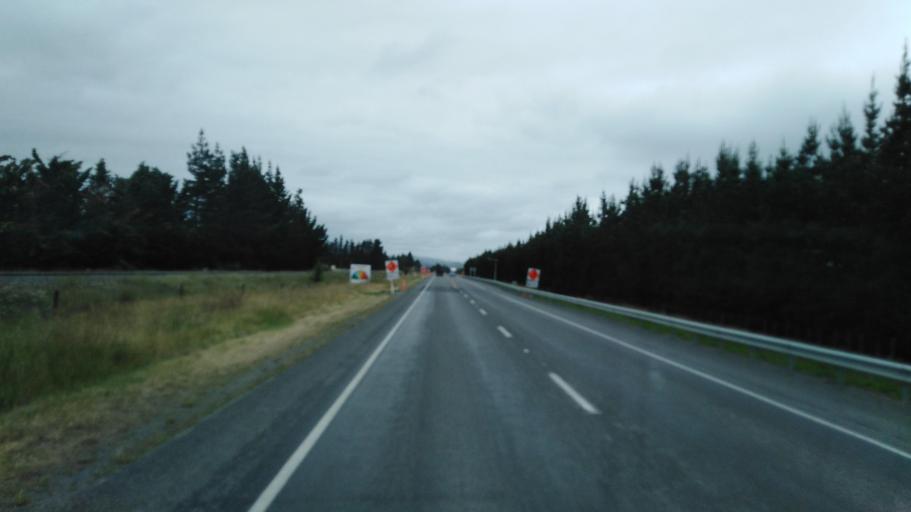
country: NZ
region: Canterbury
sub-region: Hurunui District
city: Amberley
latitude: -43.0830
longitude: 172.7440
